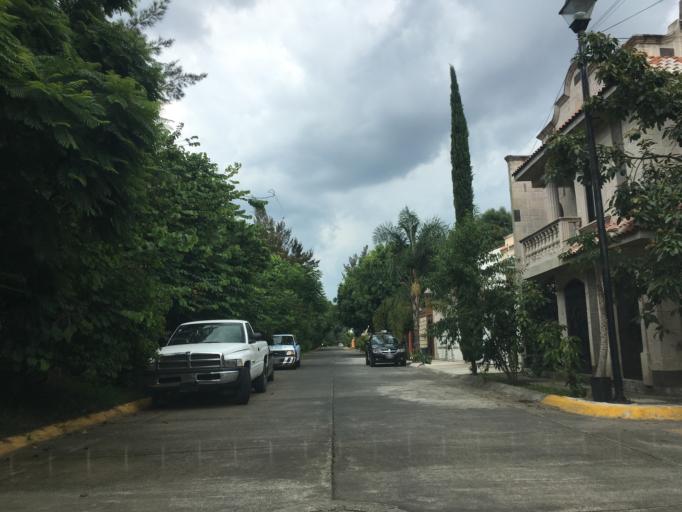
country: MX
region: Michoacan
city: Morelia
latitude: 19.6830
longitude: -101.2097
